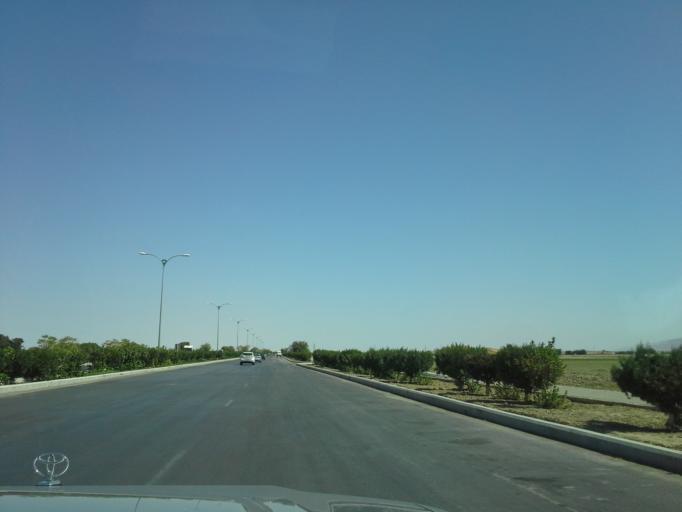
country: TM
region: Ahal
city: Annau
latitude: 37.9065
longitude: 58.5227
